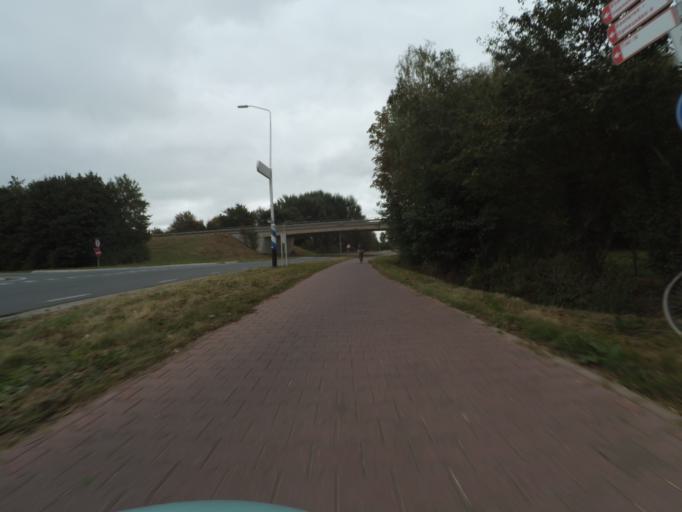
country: NL
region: Utrecht
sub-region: Gemeente Rhenen
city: Rhenen
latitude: 51.9443
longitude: 5.5704
